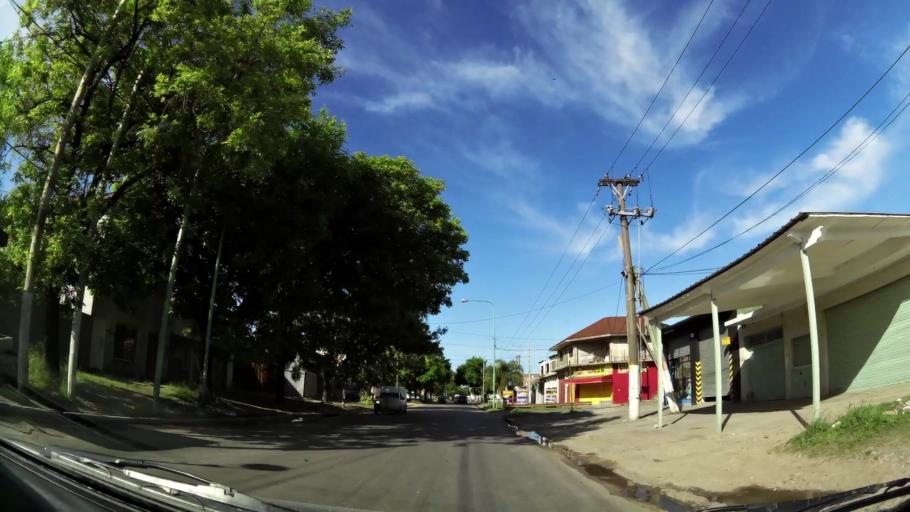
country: AR
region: Buenos Aires
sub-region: Partido de Quilmes
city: Quilmes
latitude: -34.7838
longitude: -58.2332
